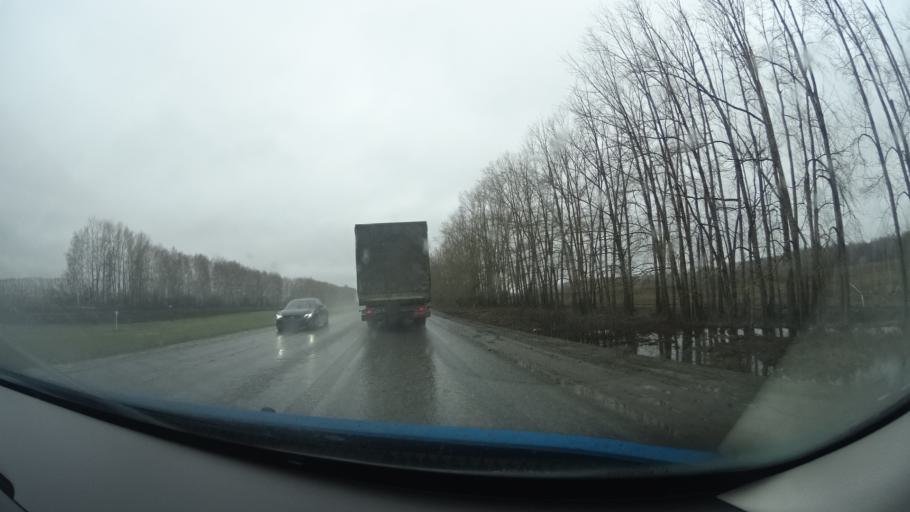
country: RU
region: Bashkortostan
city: Buzdyak
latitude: 54.6213
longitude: 54.4048
